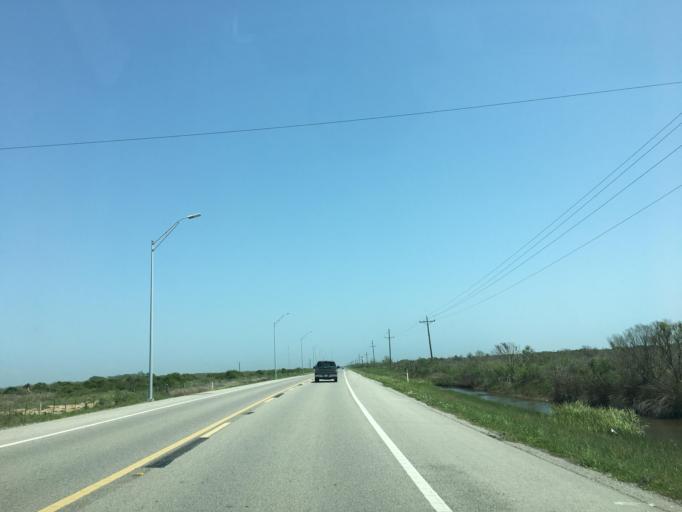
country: US
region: Texas
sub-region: Galveston County
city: Galveston
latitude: 29.3975
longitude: -94.7282
